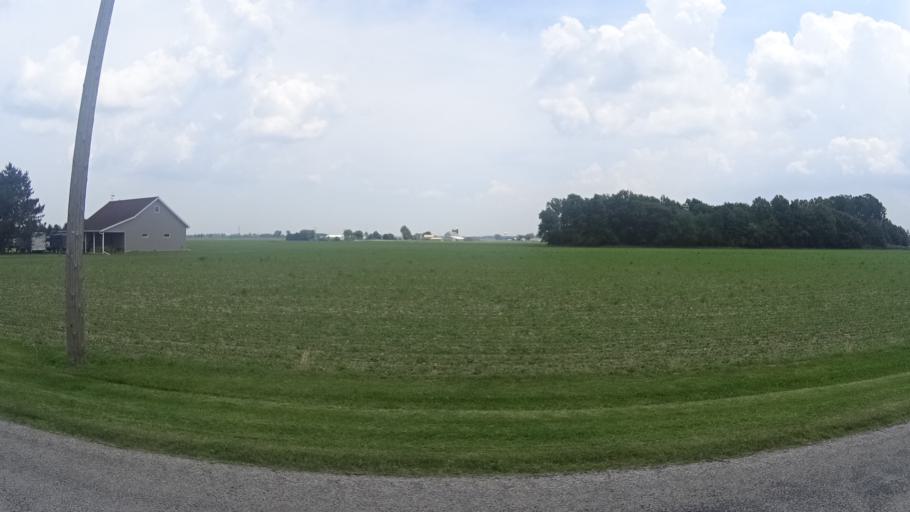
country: US
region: Ohio
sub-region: Erie County
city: Milan
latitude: 41.3189
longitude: -82.6726
